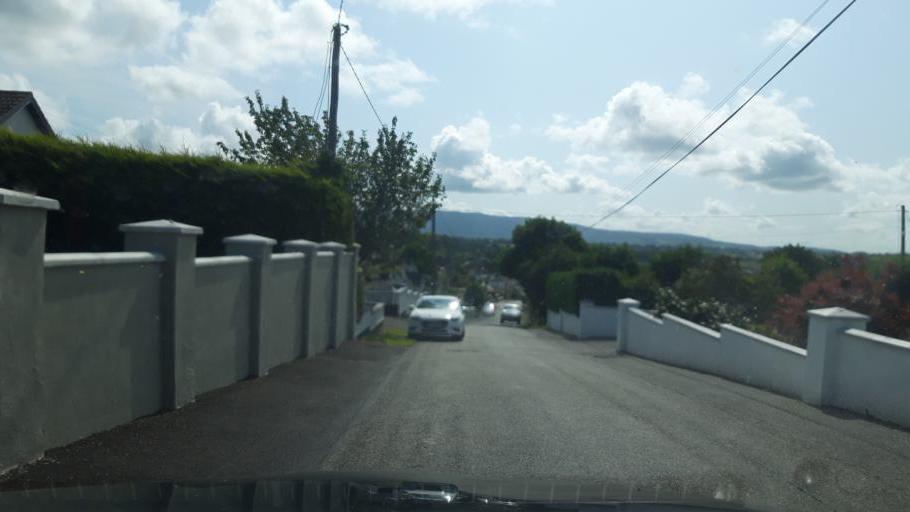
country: IE
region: Leinster
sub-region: Kilkenny
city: Graiguenamanagh
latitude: 52.5464
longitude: -6.9646
